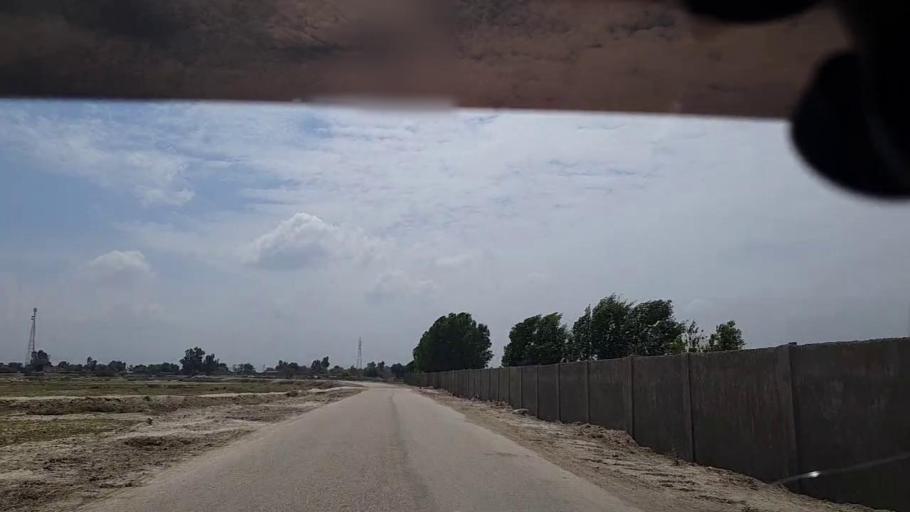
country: PK
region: Sindh
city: Ghauspur
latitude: 28.0921
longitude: 68.9600
